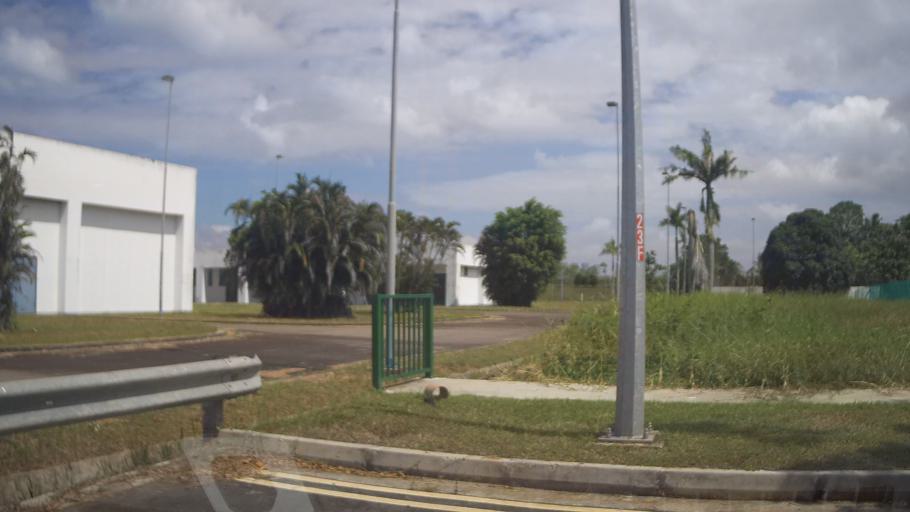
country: MY
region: Johor
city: Johor Bahru
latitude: 1.4219
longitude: 103.7254
